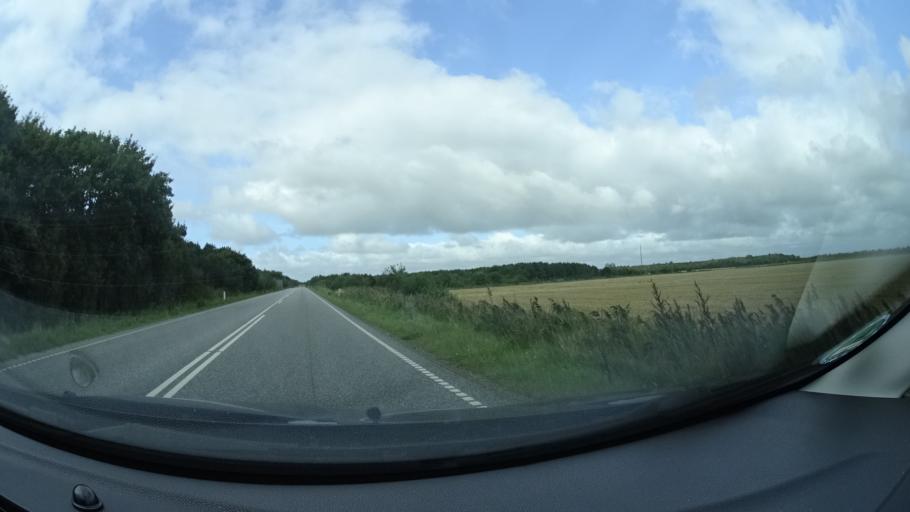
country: DK
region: Central Jutland
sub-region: Lemvig Kommune
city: Harboore
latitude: 56.6108
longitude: 8.1843
